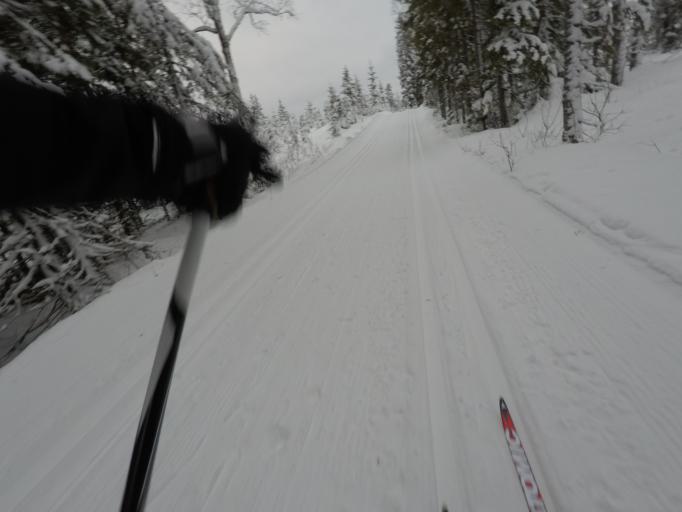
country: SE
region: Dalarna
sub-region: Ludvika Kommun
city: Abborrberget
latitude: 60.1617
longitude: 14.4825
